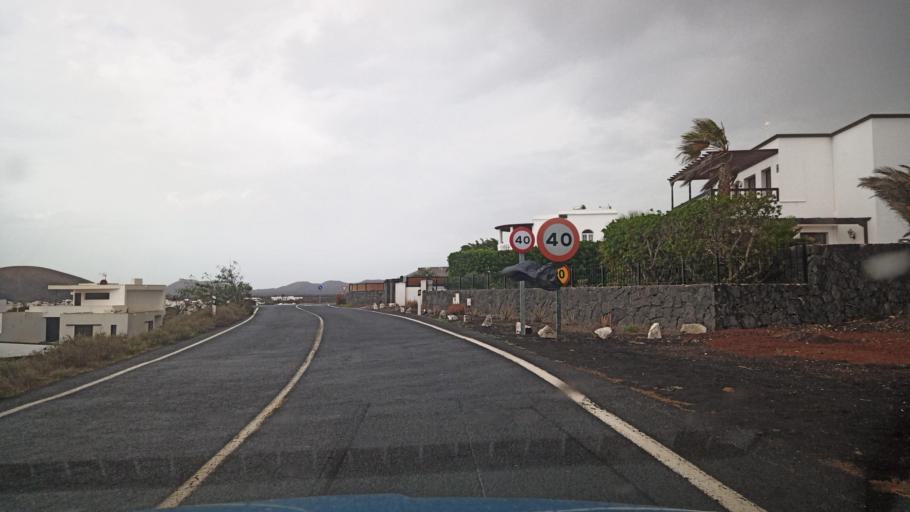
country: ES
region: Canary Islands
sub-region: Provincia de Las Palmas
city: Yaiza
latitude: 28.9464
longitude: -13.7390
